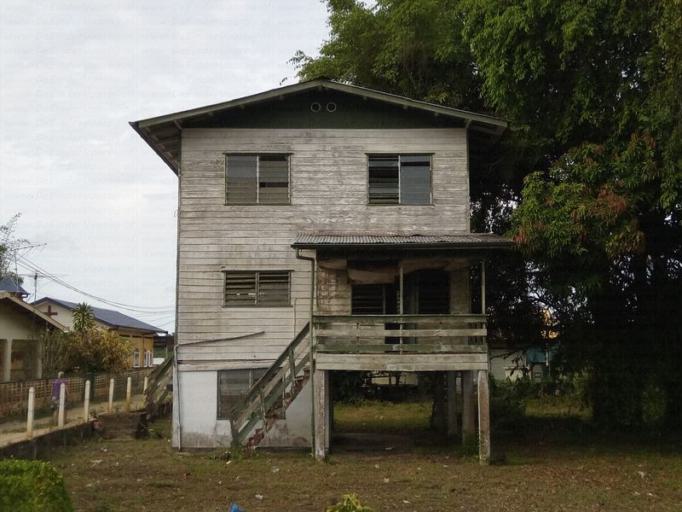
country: SR
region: Wanica
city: Lelydorp
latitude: 5.7015
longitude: -55.0818
